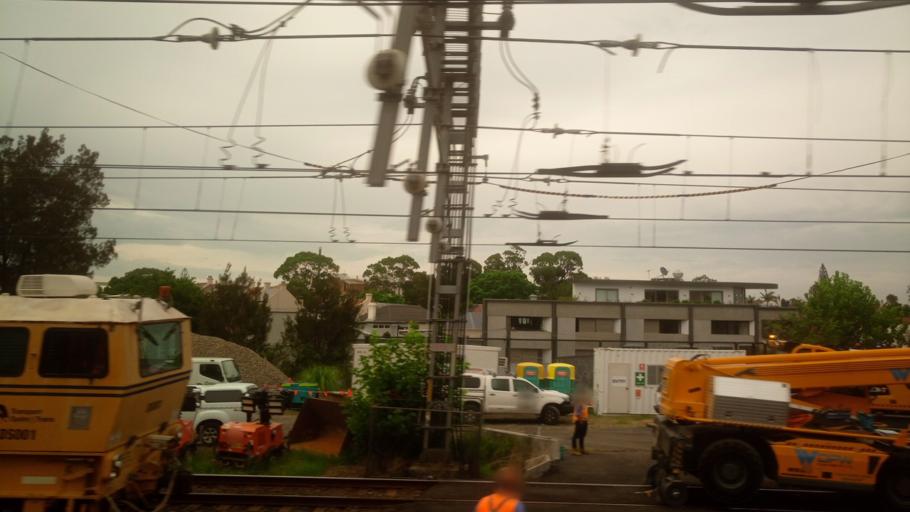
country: AU
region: New South Wales
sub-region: Marrickville
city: Newtown
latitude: -33.8966
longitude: 151.1740
